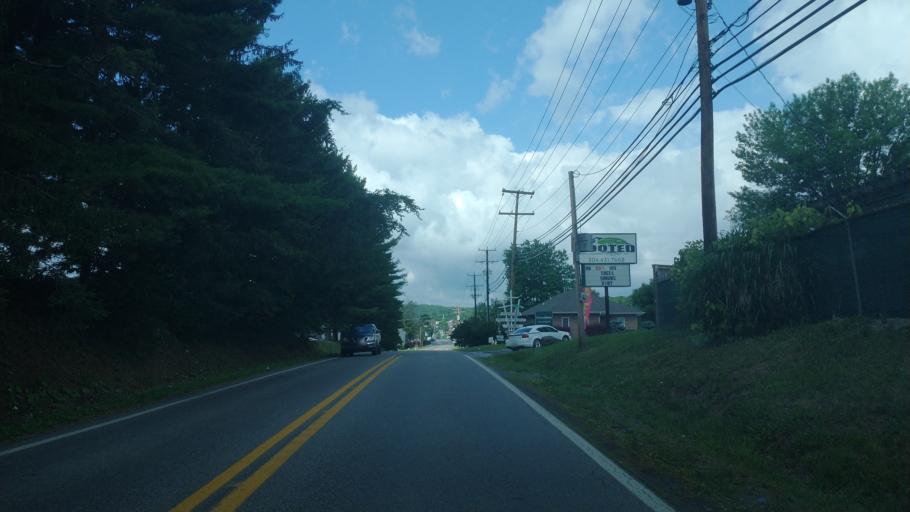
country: US
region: West Virginia
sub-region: Mercer County
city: Princeton
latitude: 37.3673
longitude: -81.1108
